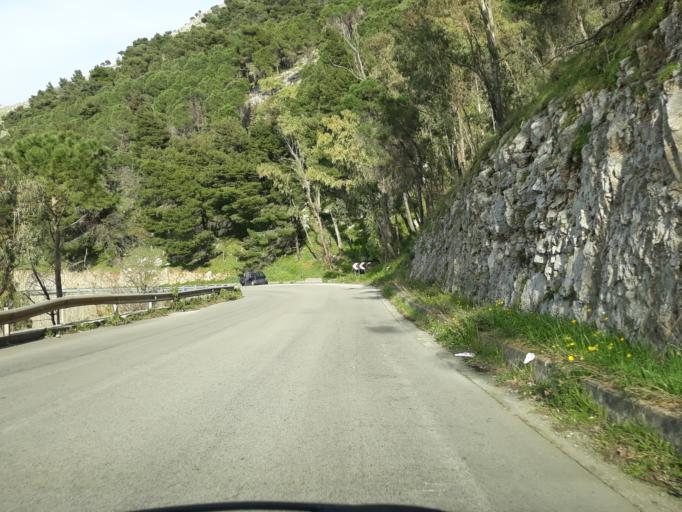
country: IT
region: Sicily
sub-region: Palermo
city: Torretta
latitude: 38.1207
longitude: 13.2449
